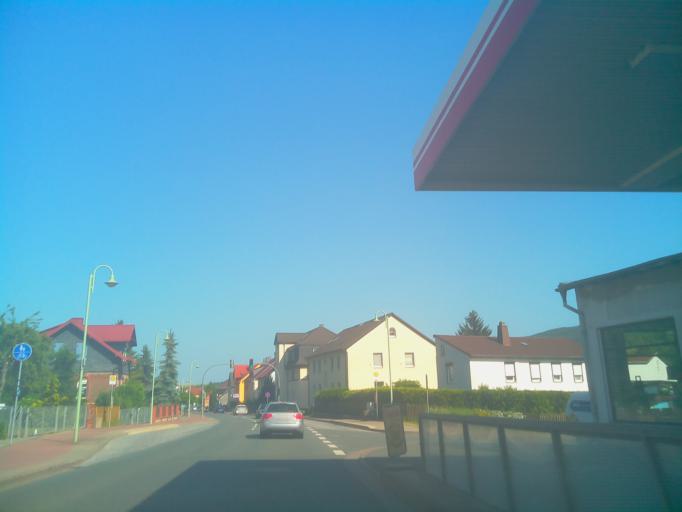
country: DE
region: Thuringia
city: Bad Blankenburg
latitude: 50.6864
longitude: 11.2529
